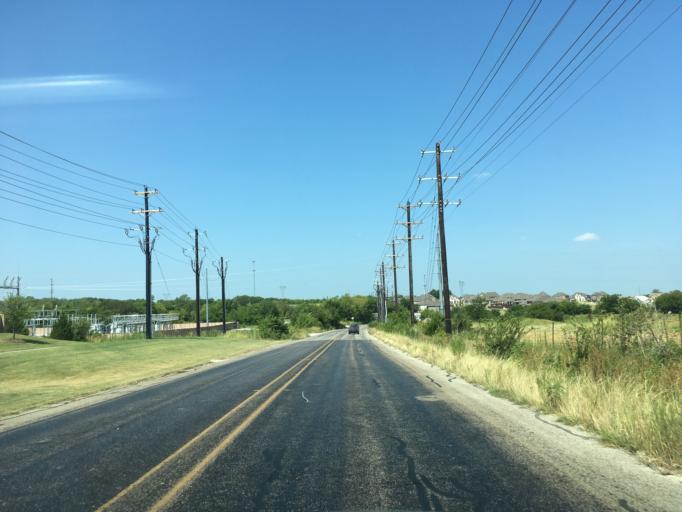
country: US
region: Texas
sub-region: Collin County
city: Prosper
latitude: 33.2039
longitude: -96.7916
